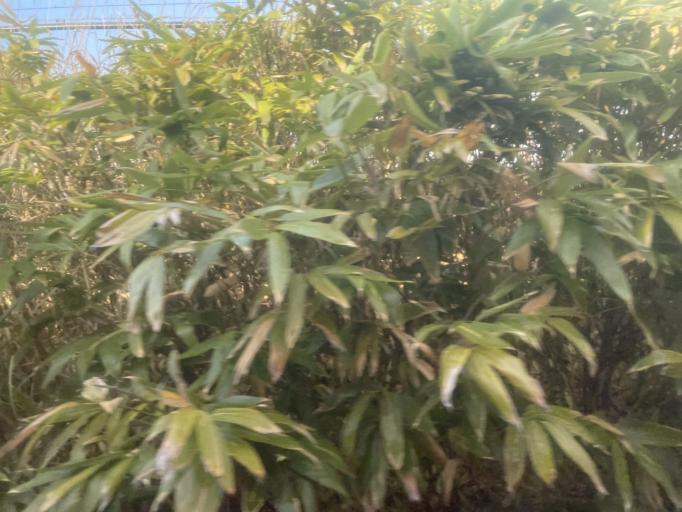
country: JP
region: Aomori
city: Goshogawara
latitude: 41.0658
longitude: 140.5658
